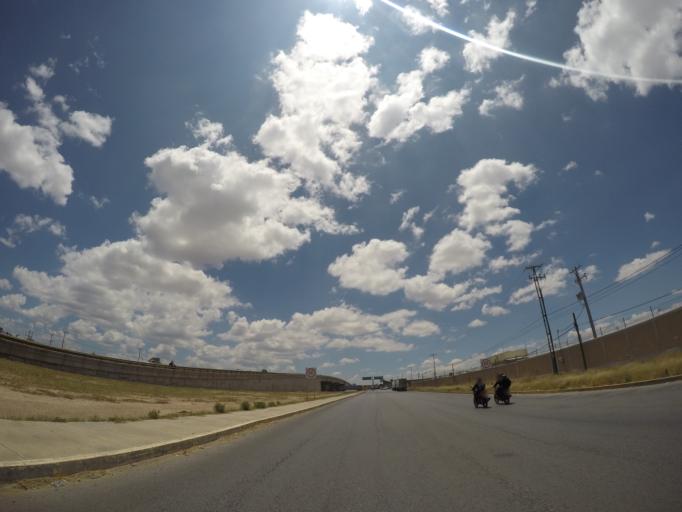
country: MX
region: San Luis Potosi
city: La Pila
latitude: 22.0442
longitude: -100.8573
